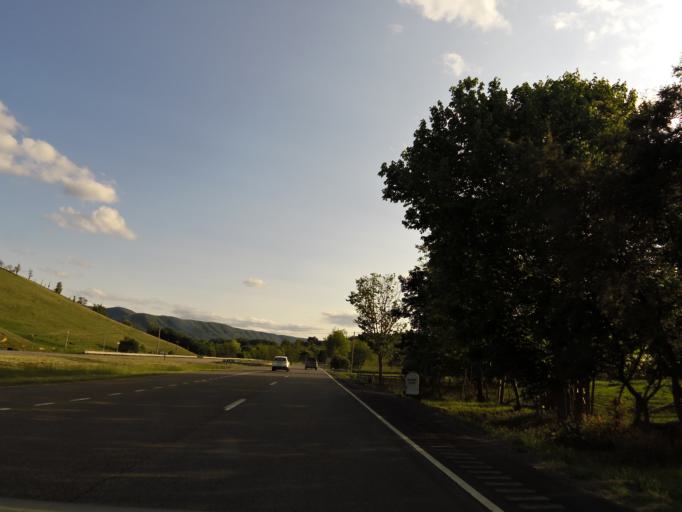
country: US
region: Virginia
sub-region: Russell County
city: Honaker
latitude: 36.9414
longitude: -81.9621
